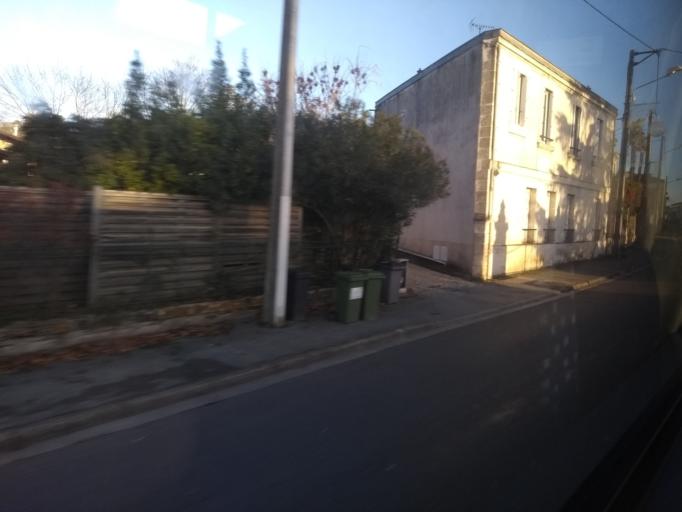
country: FR
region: Aquitaine
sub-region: Departement de la Gironde
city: Gradignan
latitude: 44.7705
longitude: -0.6157
